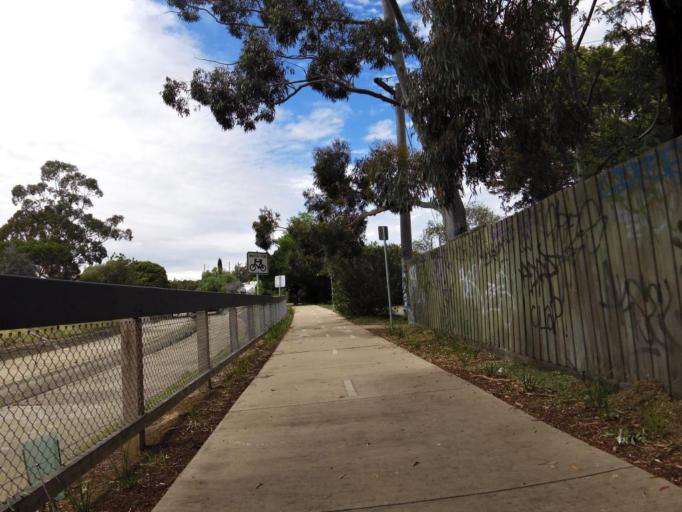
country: AU
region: Victoria
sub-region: Glen Eira
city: Elsternwick
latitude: -37.8942
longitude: 145.0026
